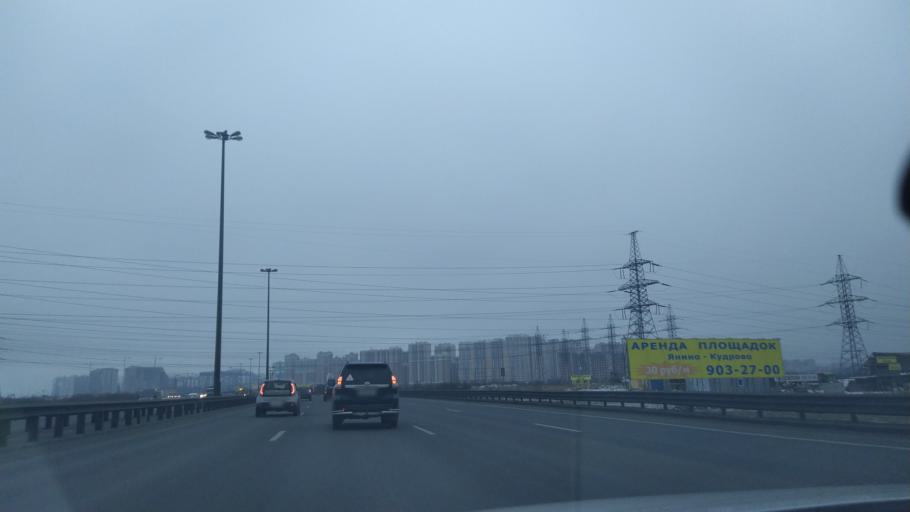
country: RU
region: St.-Petersburg
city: Krasnogvargeisky
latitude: 59.9257
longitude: 30.5312
